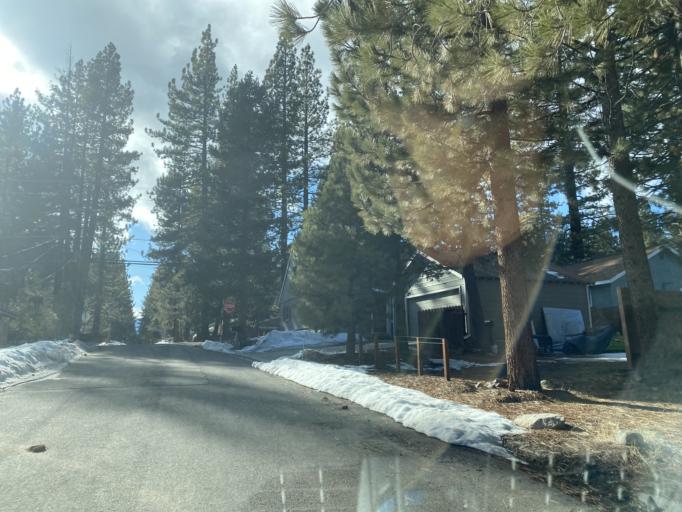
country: US
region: California
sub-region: El Dorado County
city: South Lake Tahoe
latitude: 38.9222
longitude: -119.9754
